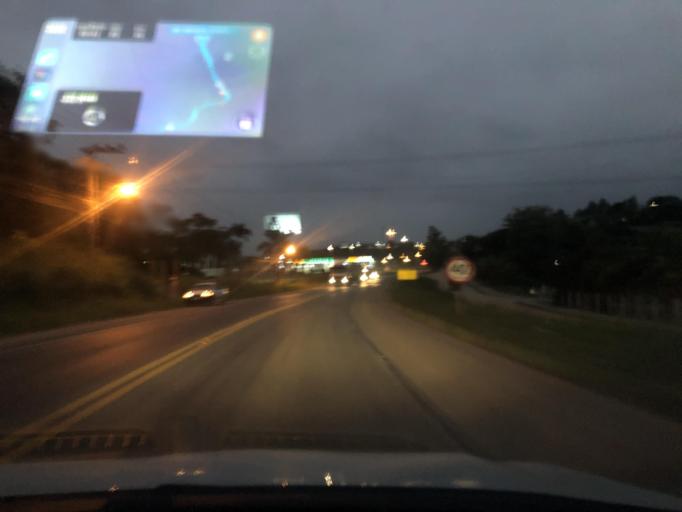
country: BR
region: Santa Catarina
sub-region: Guaramirim
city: Guaramirim
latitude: -26.5872
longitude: -48.9865
